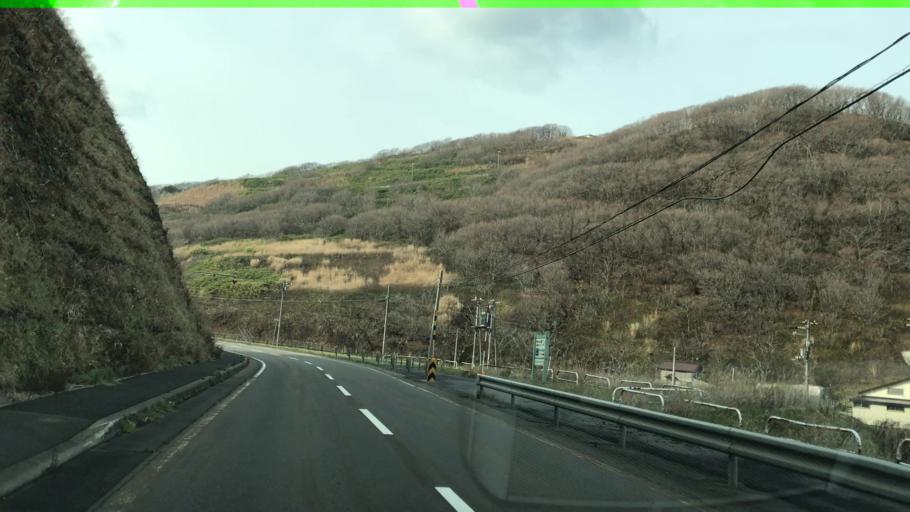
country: JP
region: Hokkaido
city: Iwanai
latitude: 43.3296
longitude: 140.3670
